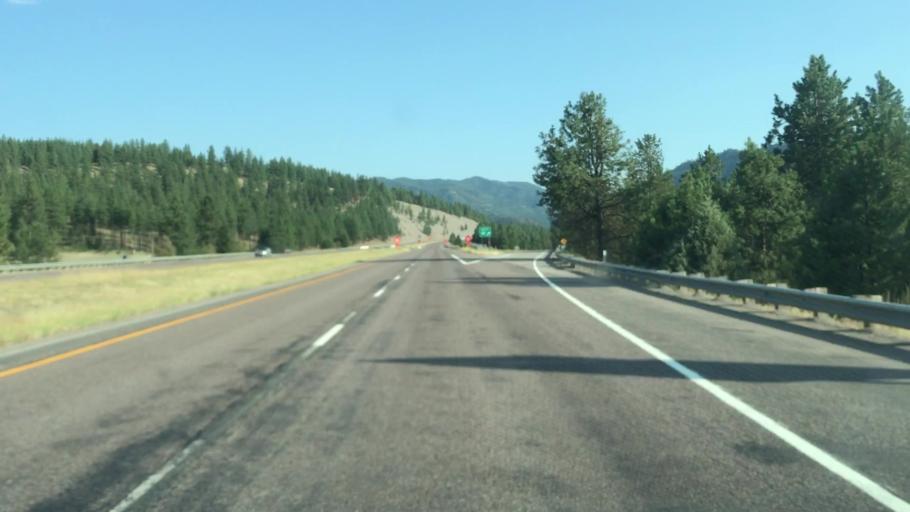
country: US
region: Montana
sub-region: Mineral County
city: Superior
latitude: 47.0289
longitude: -114.7414
